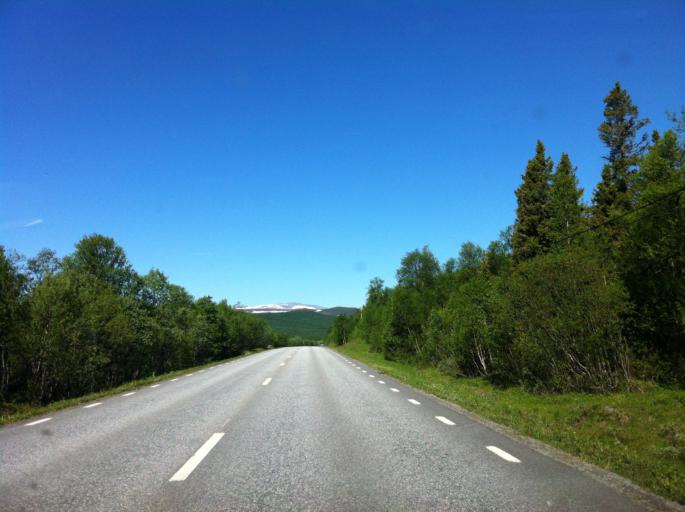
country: NO
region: Hedmark
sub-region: Engerdal
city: Engerdal
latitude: 62.5344
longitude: 12.3732
